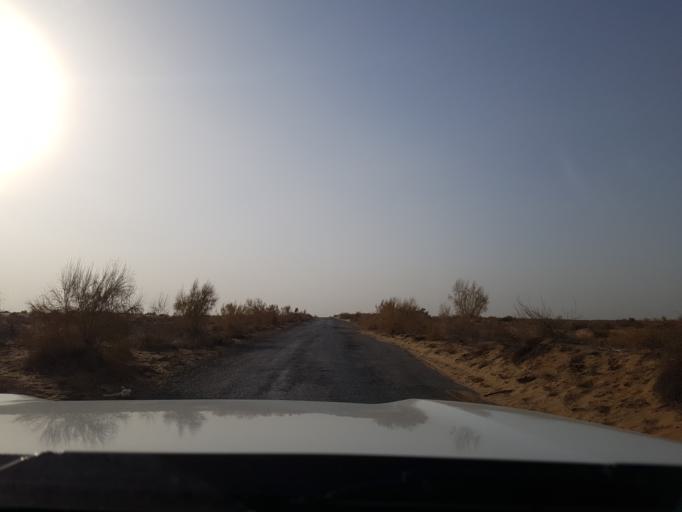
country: UZ
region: Xorazm
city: Hazorasp
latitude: 41.1952
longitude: 60.9244
